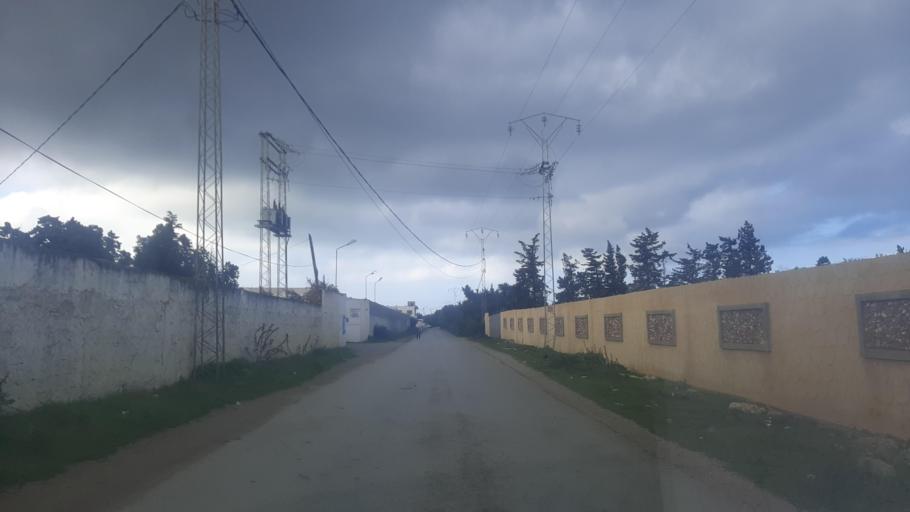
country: TN
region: Nabul
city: Manzil Bu Zalafah
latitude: 36.7320
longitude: 10.5378
